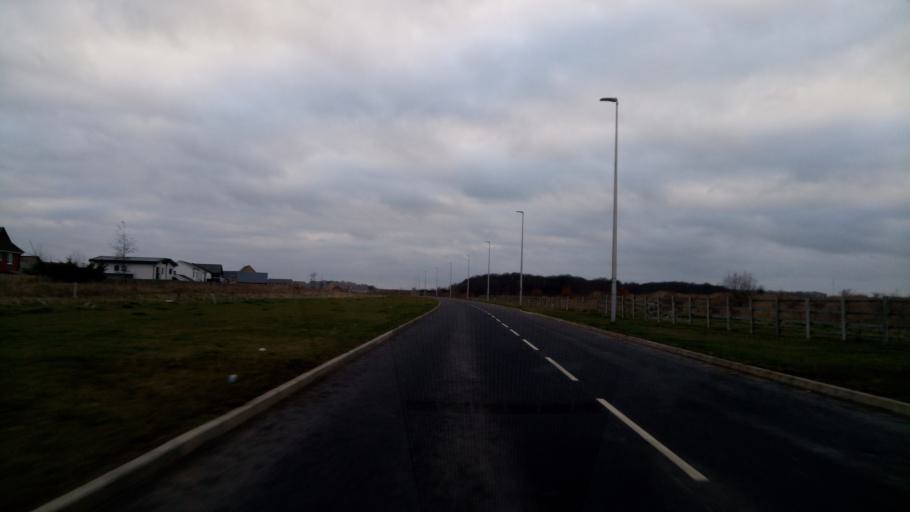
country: GB
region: England
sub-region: Cambridgeshire
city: Yaxley
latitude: 52.5338
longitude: -0.2841
